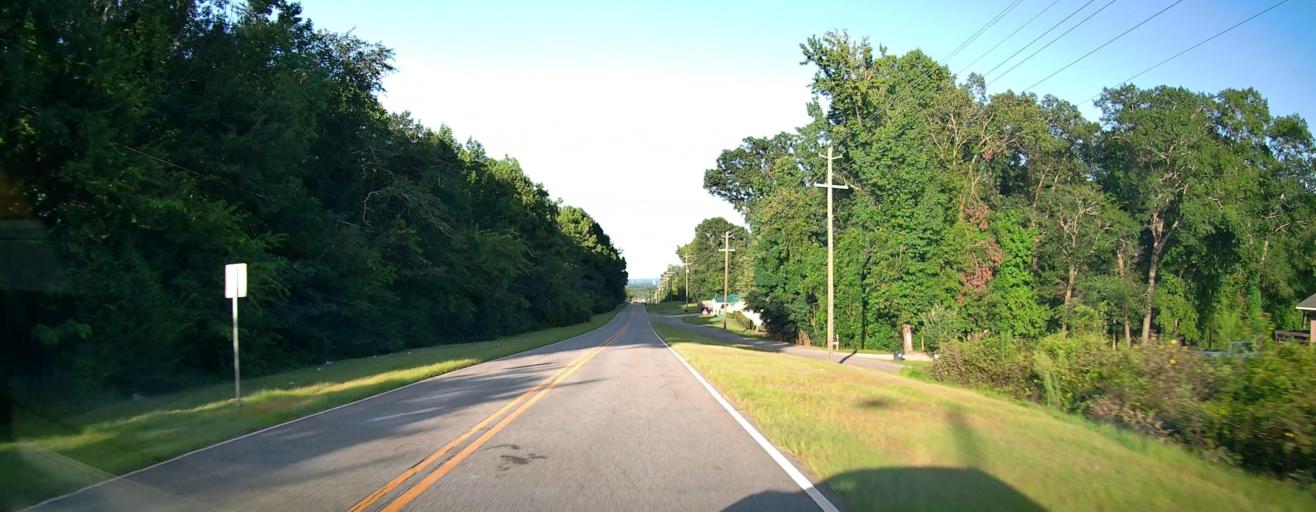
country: US
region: Alabama
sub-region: Russell County
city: Phenix City
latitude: 32.4226
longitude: -85.0280
